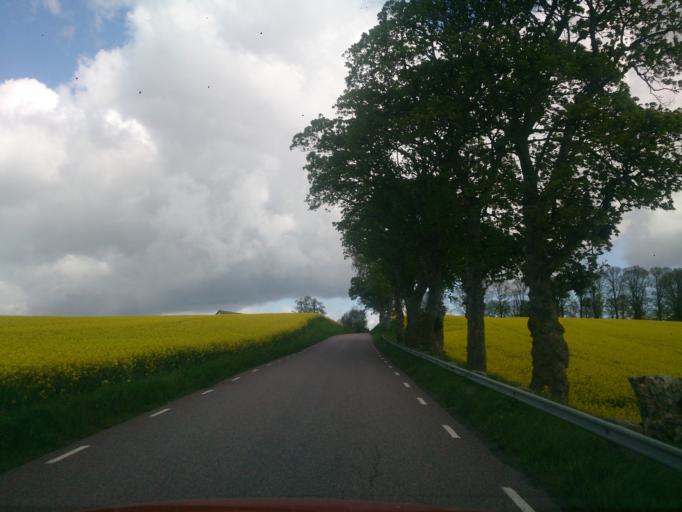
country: SE
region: Skane
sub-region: Ystads Kommun
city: Ystad
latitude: 55.4598
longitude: 13.7071
